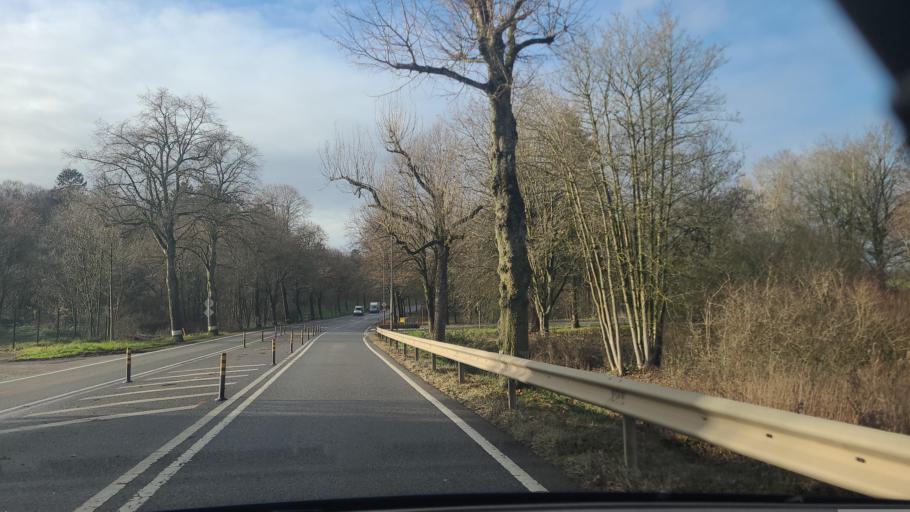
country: LU
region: Luxembourg
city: Schouweiler
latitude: 49.5745
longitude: 5.9422
